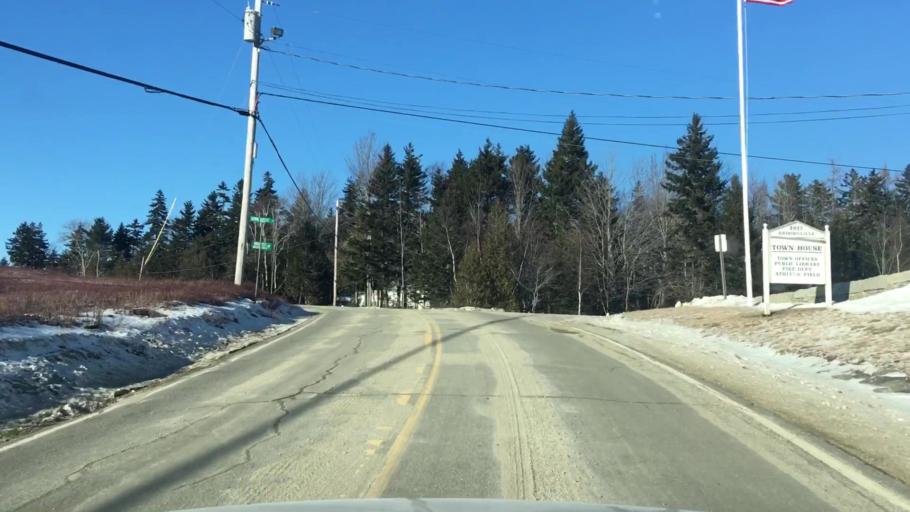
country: US
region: Maine
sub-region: Hancock County
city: Castine
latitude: 44.3636
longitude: -68.7499
